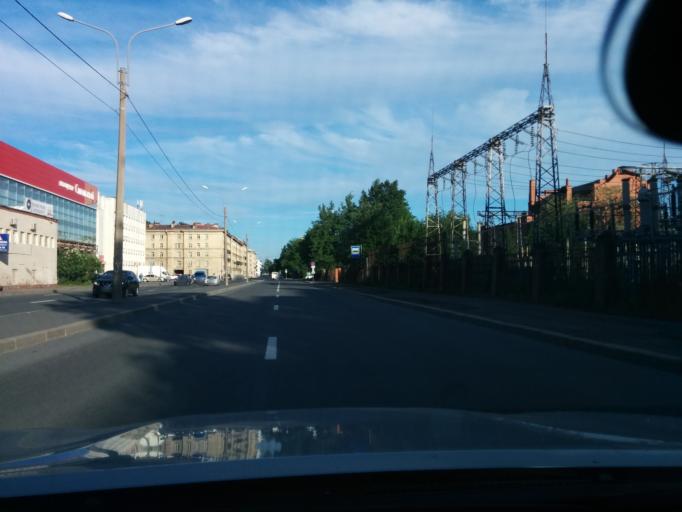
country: RU
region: Leningrad
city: Finlyandskiy
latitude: 59.9728
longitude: 30.3799
